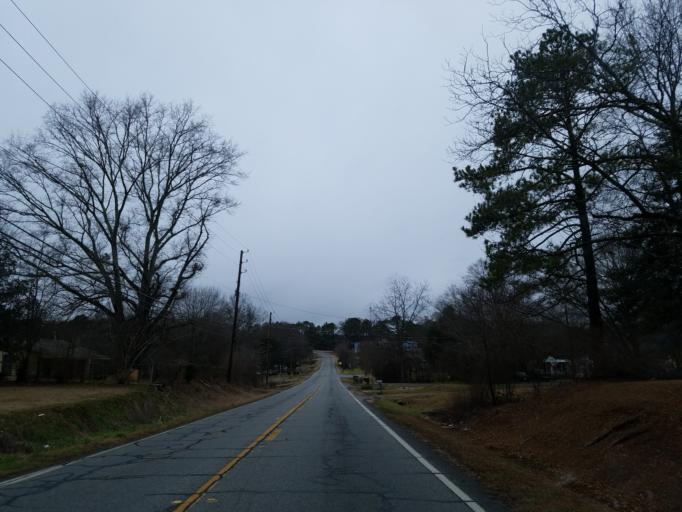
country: US
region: Georgia
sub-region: Bartow County
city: Cartersville
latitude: 34.2083
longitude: -84.8326
